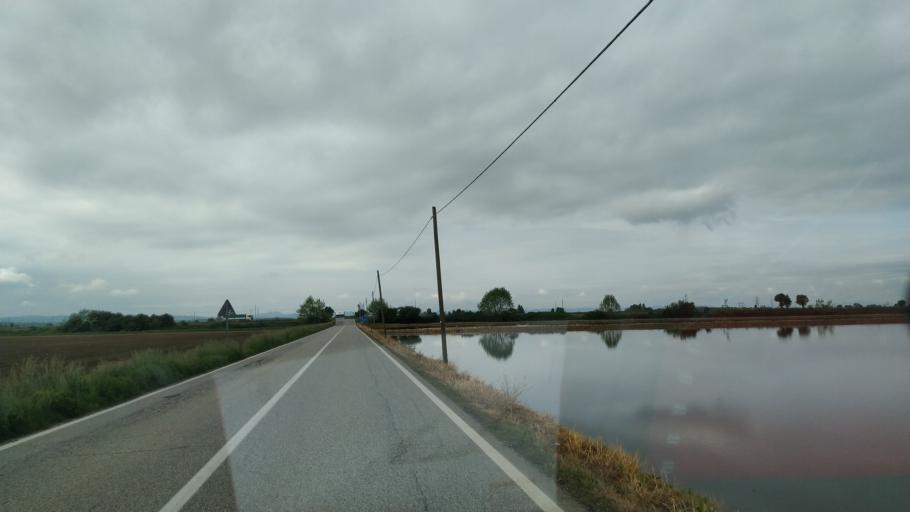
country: IT
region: Piedmont
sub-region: Provincia di Vercelli
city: Ronsecco
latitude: 45.2719
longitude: 8.2543
